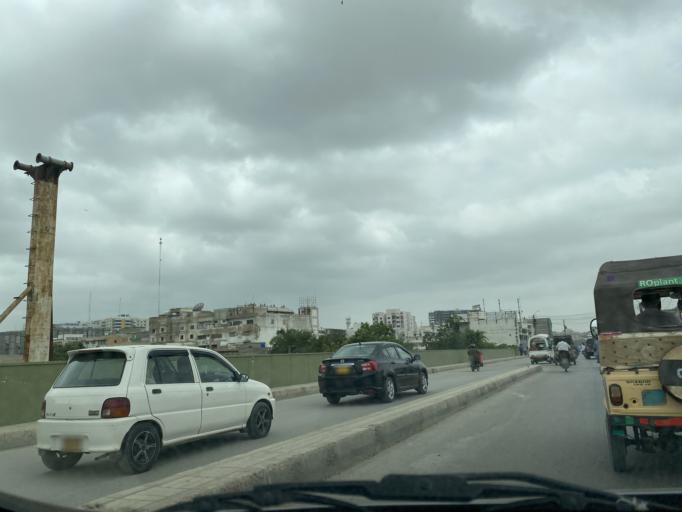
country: PK
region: Sindh
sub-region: Karachi District
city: Karachi
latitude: 24.8659
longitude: 67.0840
